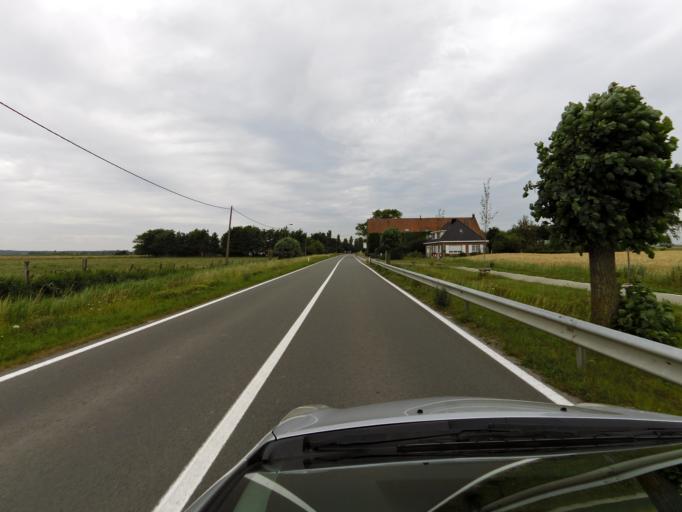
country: BE
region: Flanders
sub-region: Provincie West-Vlaanderen
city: Wenduine
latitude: 51.2734
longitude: 3.0909
